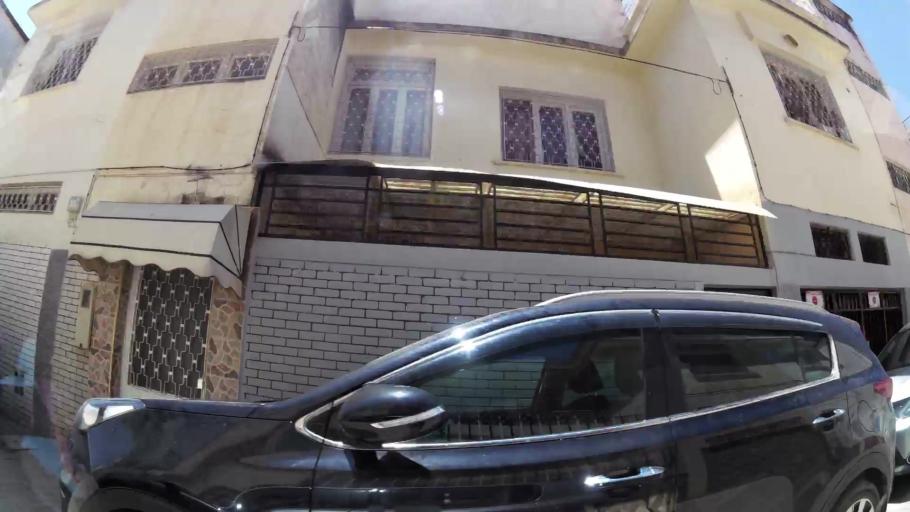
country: MA
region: Fes-Boulemane
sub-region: Fes
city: Fes
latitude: 34.0259
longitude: -5.0061
